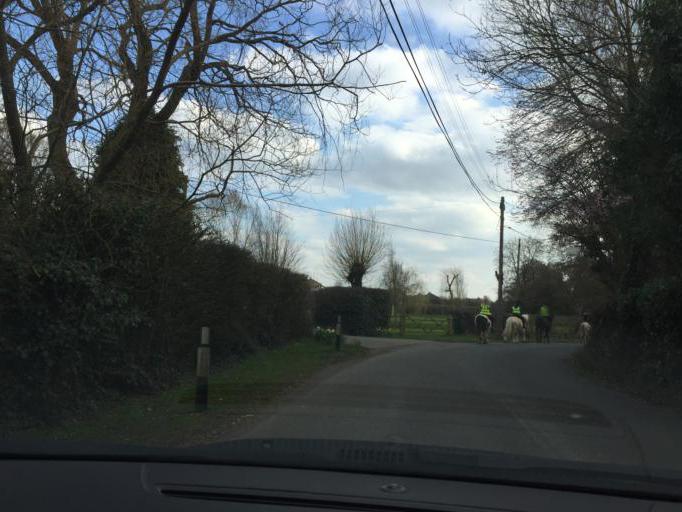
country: GB
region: England
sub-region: Coventry
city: Keresley
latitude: 52.4360
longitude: -1.5695
